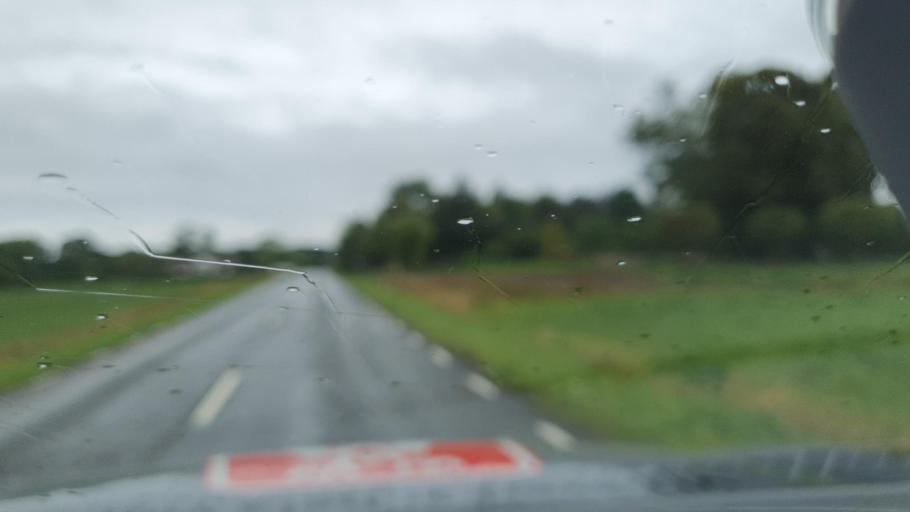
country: SE
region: Skane
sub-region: Simrishamns Kommun
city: Kivik
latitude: 55.5730
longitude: 14.1505
